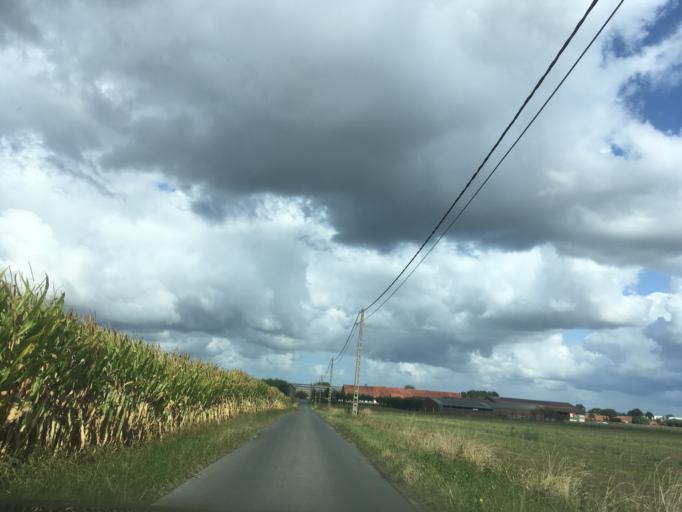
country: BE
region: Flanders
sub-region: Provincie West-Vlaanderen
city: Kortemark
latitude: 51.0072
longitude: 3.0332
